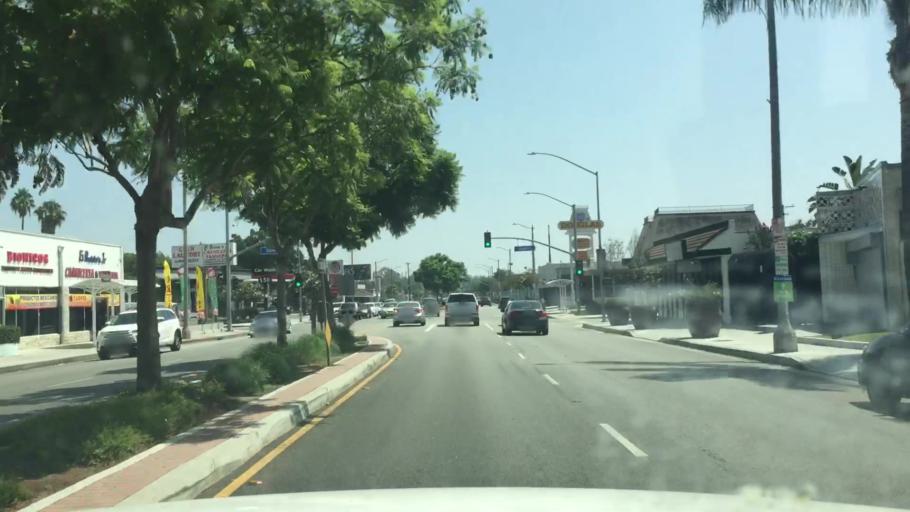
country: US
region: California
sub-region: Los Angeles County
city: East Rancho Dominguez
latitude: 33.8510
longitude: -118.1955
